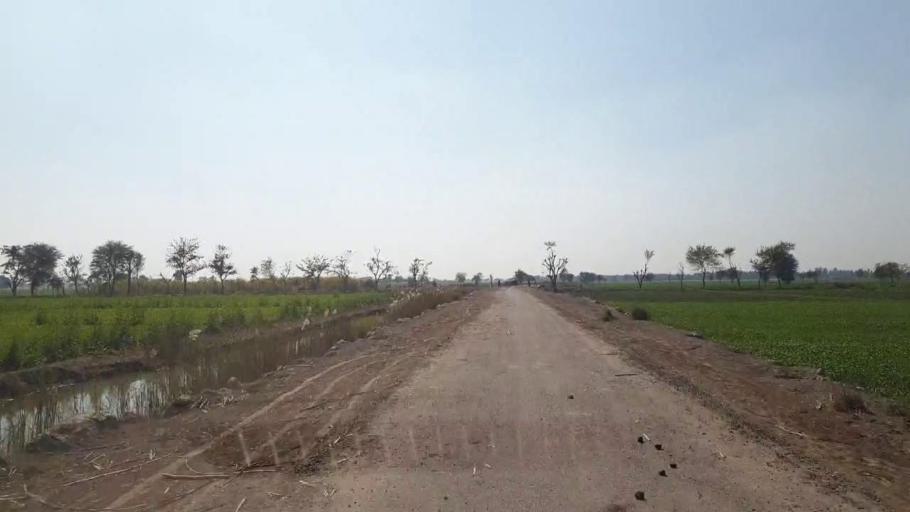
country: PK
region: Sindh
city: Bhit Shah
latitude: 25.9280
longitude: 68.4785
